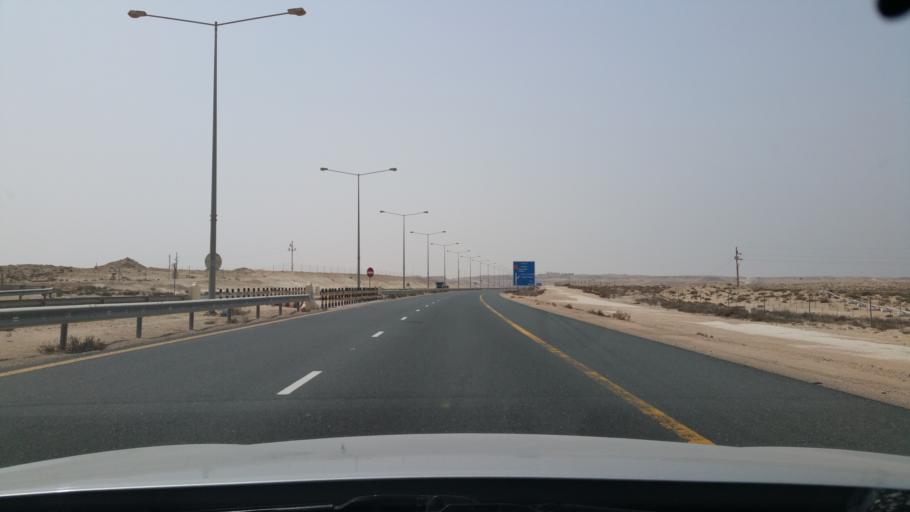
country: QA
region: Baladiyat ar Rayyan
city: Dukhan
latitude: 25.3460
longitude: 50.7826
